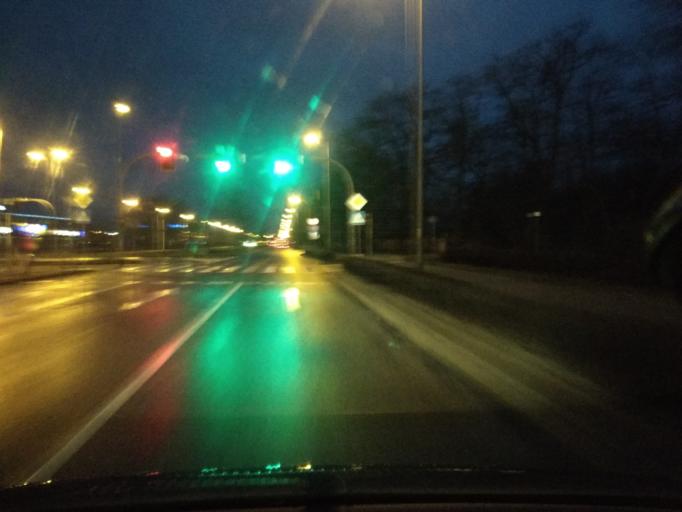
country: PL
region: Lower Silesian Voivodeship
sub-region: Powiat wroclawski
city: Wroclaw
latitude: 51.1309
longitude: 16.9673
